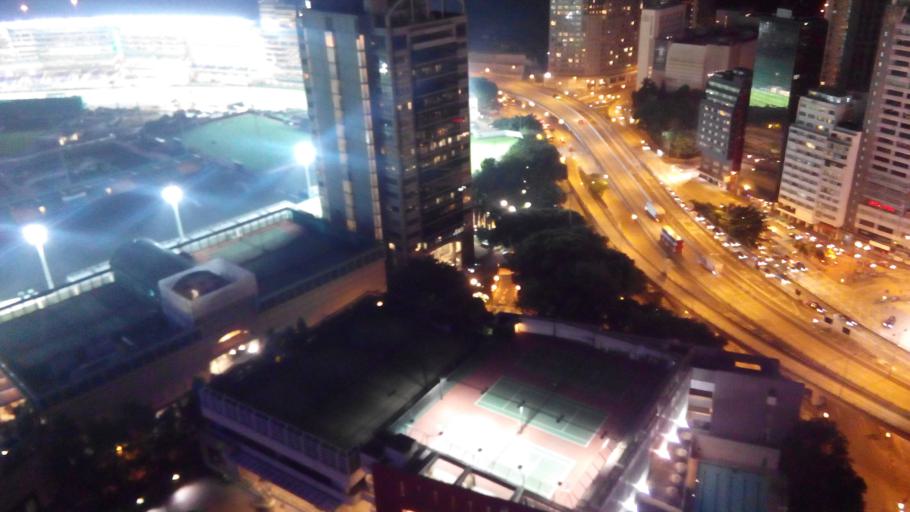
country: HK
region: Wanchai
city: Wan Chai
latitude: 22.2767
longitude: 114.1826
